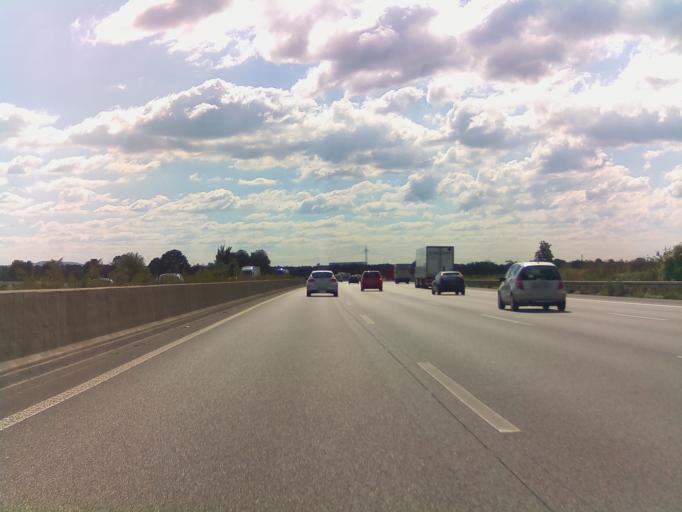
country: DE
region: Hesse
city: Weiterstadt
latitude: 49.9309
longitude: 8.6132
